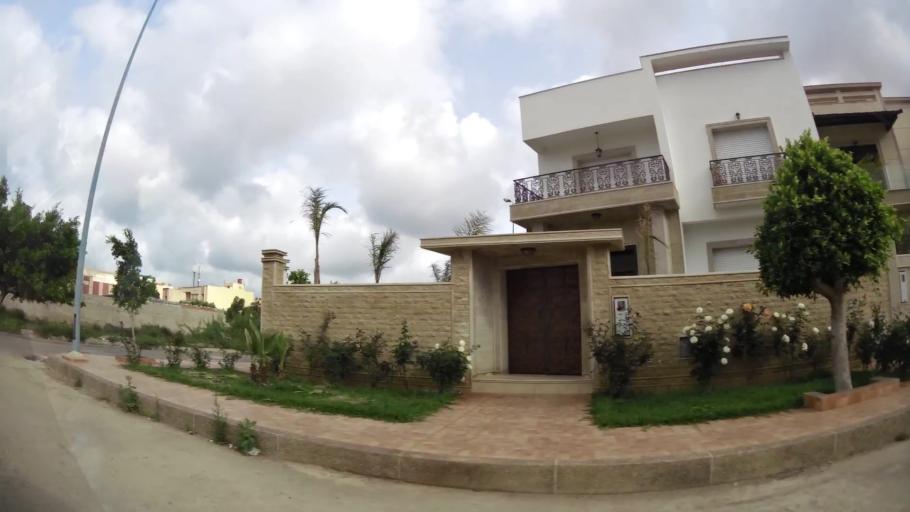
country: MA
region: Oriental
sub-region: Nador
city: Nador
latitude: 35.1636
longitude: -2.9146
